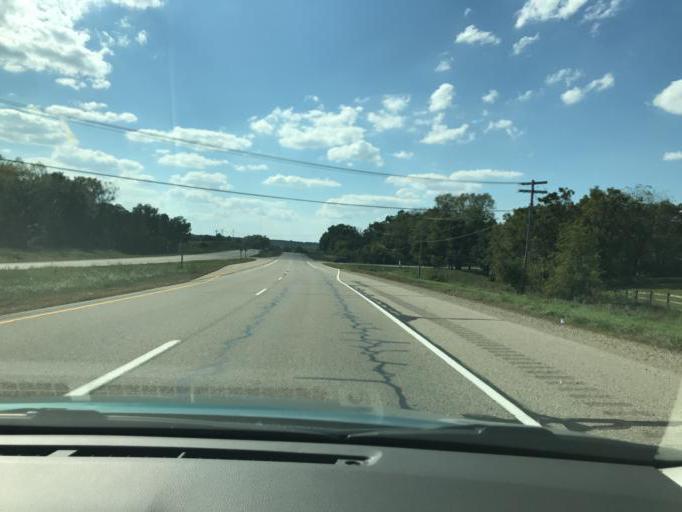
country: US
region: Wisconsin
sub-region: Walworth County
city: Lake Geneva
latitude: 42.5967
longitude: -88.3802
